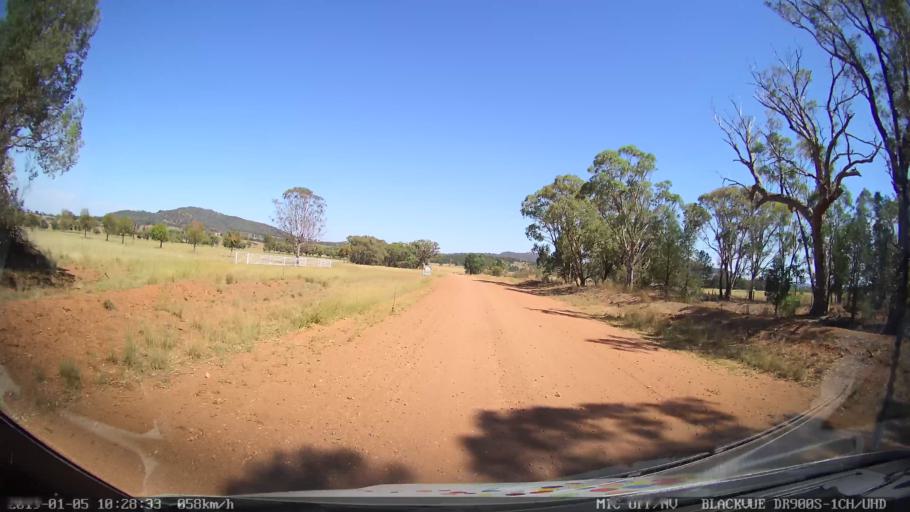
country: AU
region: New South Wales
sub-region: Gilgandra
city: Gilgandra
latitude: -31.5444
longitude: 148.9377
